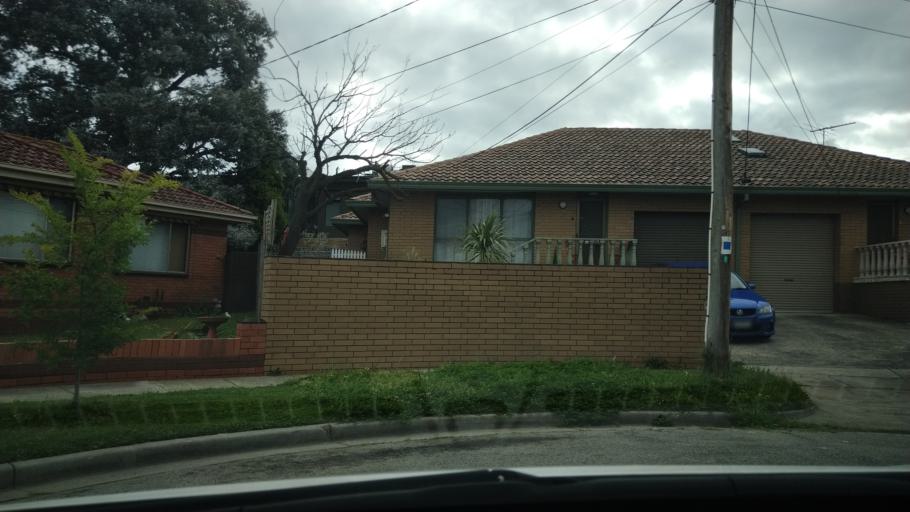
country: AU
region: Victoria
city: Highett
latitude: -37.9561
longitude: 145.0702
